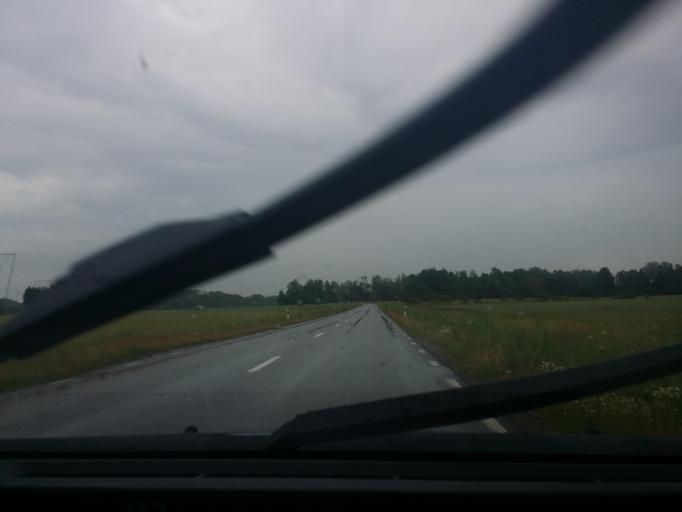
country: SE
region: OErebro
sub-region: Lindesbergs Kommun
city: Fellingsbro
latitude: 59.4266
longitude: 15.6108
